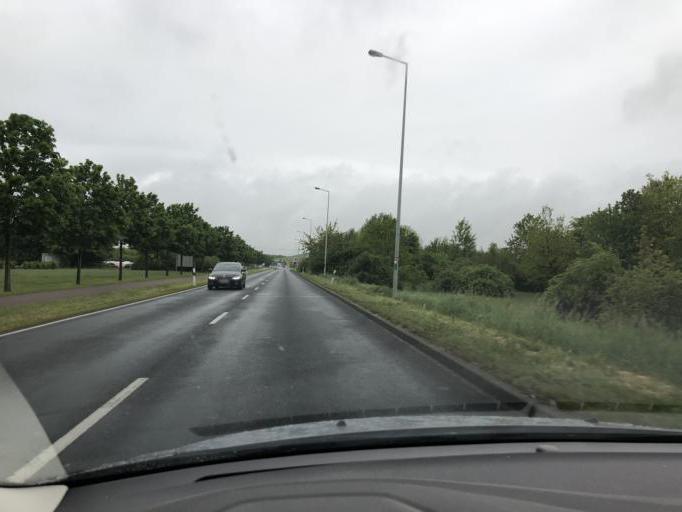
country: DE
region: Saxony-Anhalt
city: Dessau
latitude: 51.8166
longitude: 12.2157
